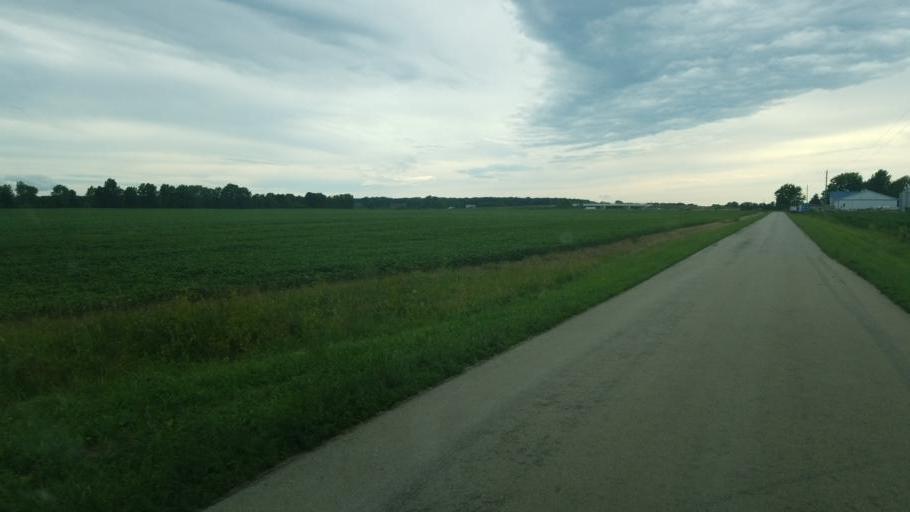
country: US
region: Ohio
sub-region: Delaware County
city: Sunbury
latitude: 40.3152
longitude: -82.9025
